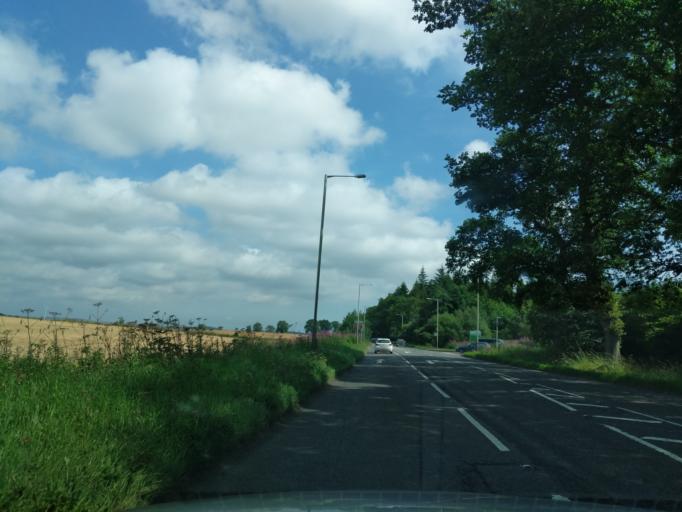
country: GB
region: Scotland
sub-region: Angus
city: Muirhead
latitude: 56.5050
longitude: -3.1327
